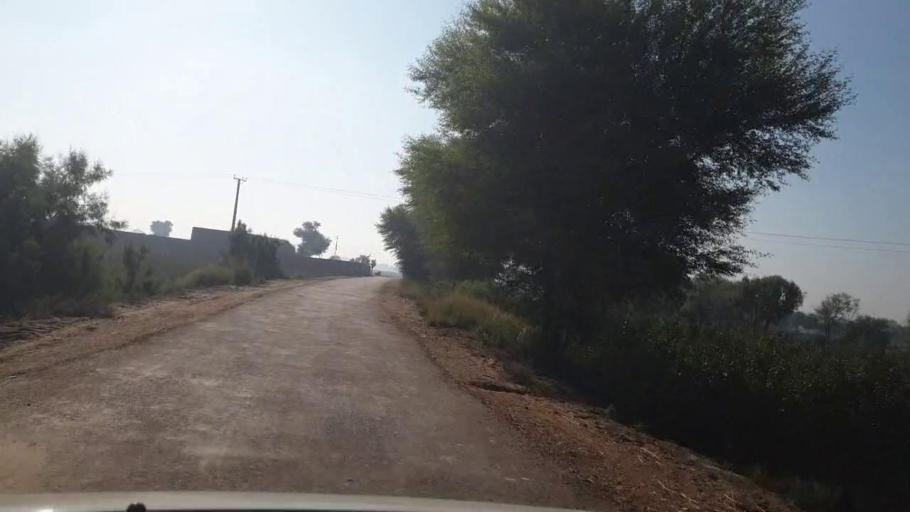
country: PK
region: Sindh
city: Dadu
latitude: 26.6561
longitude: 67.8223
